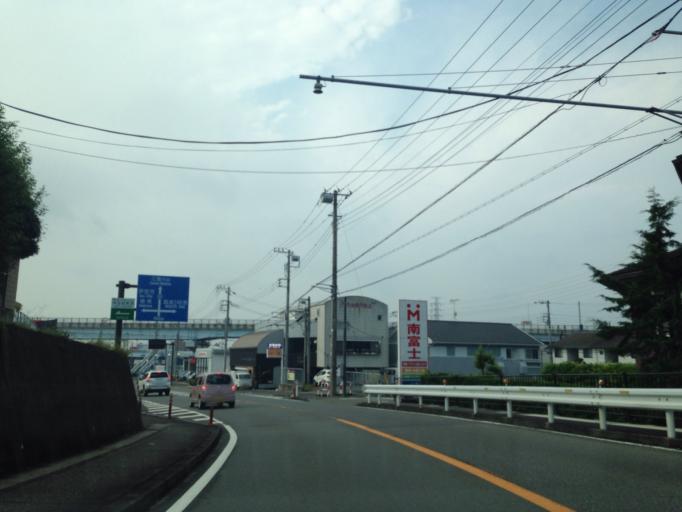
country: JP
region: Shizuoka
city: Mishima
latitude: 35.1514
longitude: 138.9071
